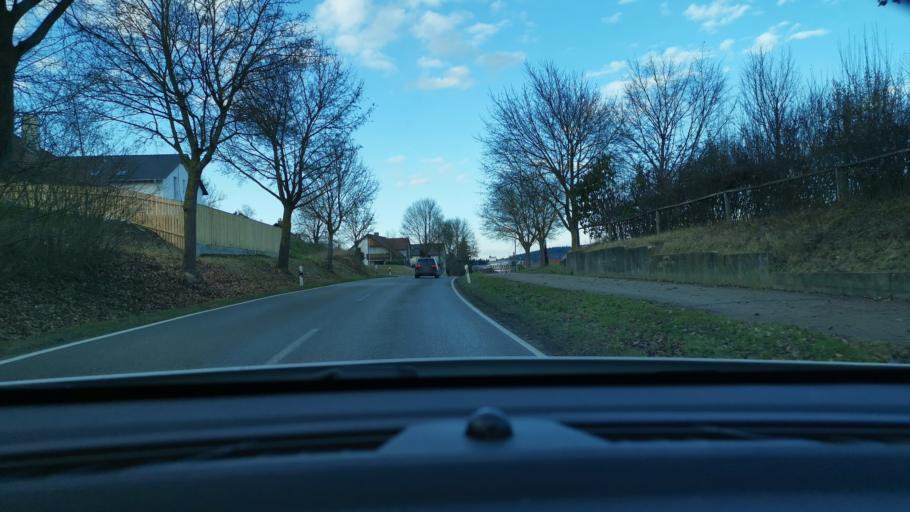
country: DE
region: Bavaria
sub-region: Swabia
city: Holzheim
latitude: 48.5856
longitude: 10.9615
